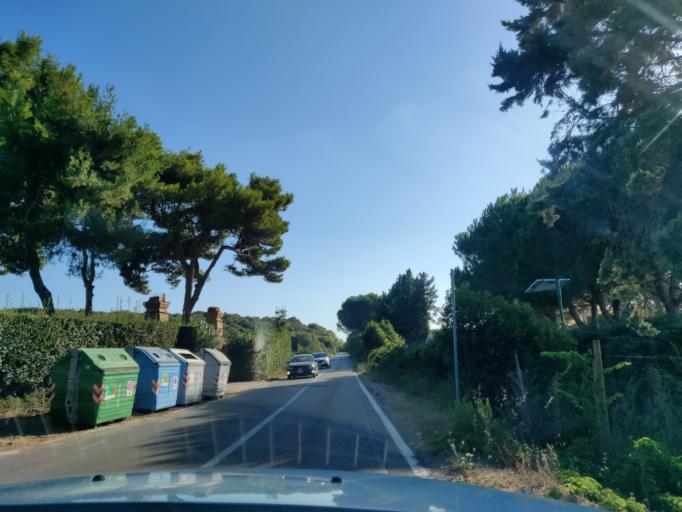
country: IT
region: Tuscany
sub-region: Provincia di Grosseto
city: Orbetello Scalo
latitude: 42.4293
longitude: 11.2845
